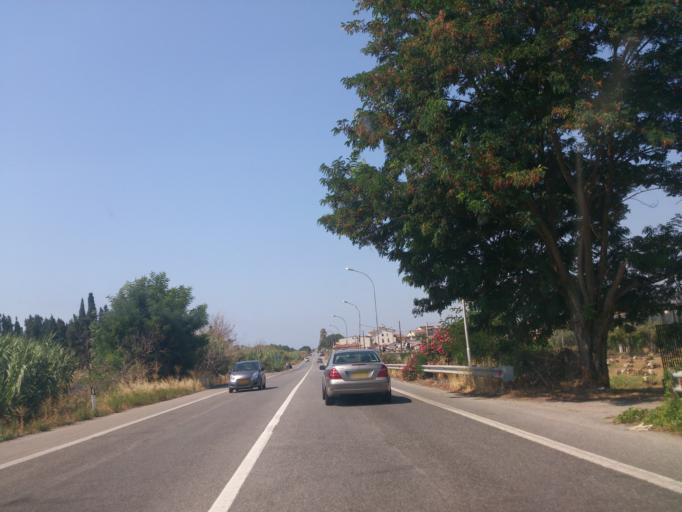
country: IT
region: Calabria
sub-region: Provincia di Reggio Calabria
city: Caulonia Marina
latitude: 38.3543
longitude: 16.4819
